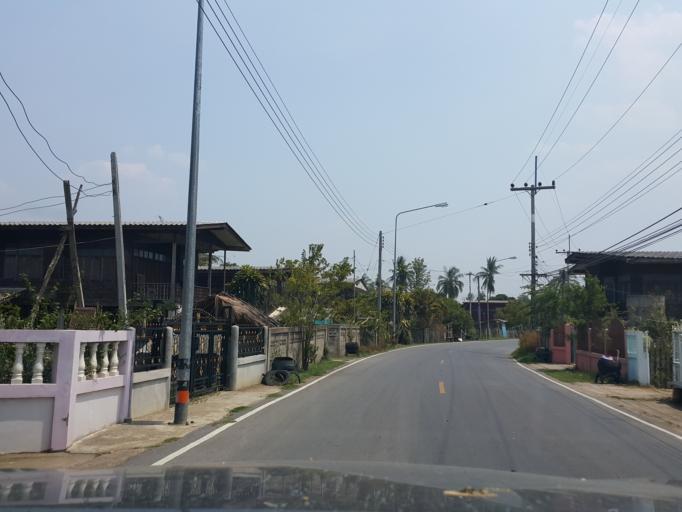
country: TH
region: Lampang
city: Mae Phrik
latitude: 17.4987
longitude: 99.1280
